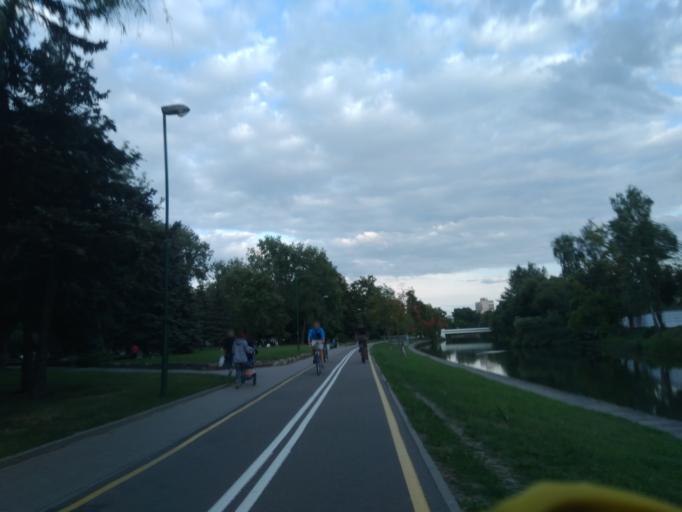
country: BY
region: Minsk
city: Minsk
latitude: 53.8964
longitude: 27.5789
